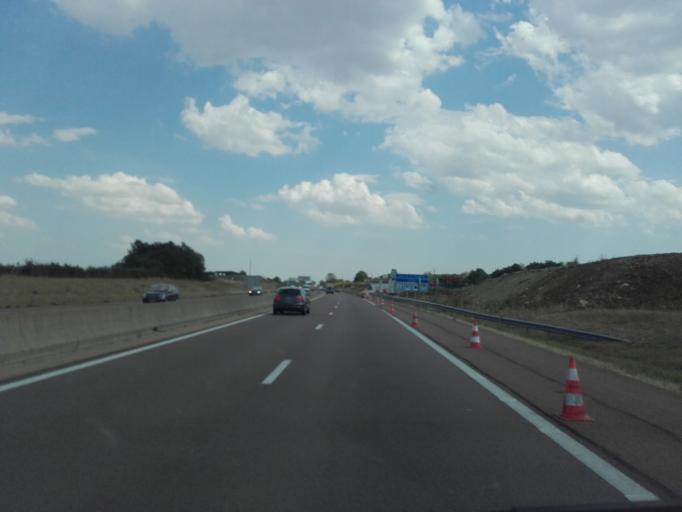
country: FR
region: Bourgogne
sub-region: Departement de l'Yonne
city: Avallon
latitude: 47.5048
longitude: 4.0166
